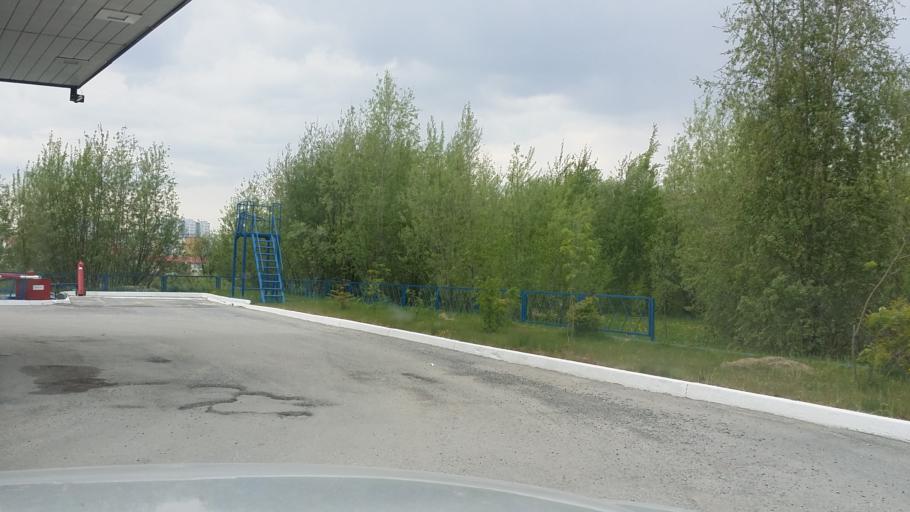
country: RU
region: Khanty-Mansiyskiy Avtonomnyy Okrug
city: Nizhnevartovsk
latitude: 60.9389
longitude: 76.6081
